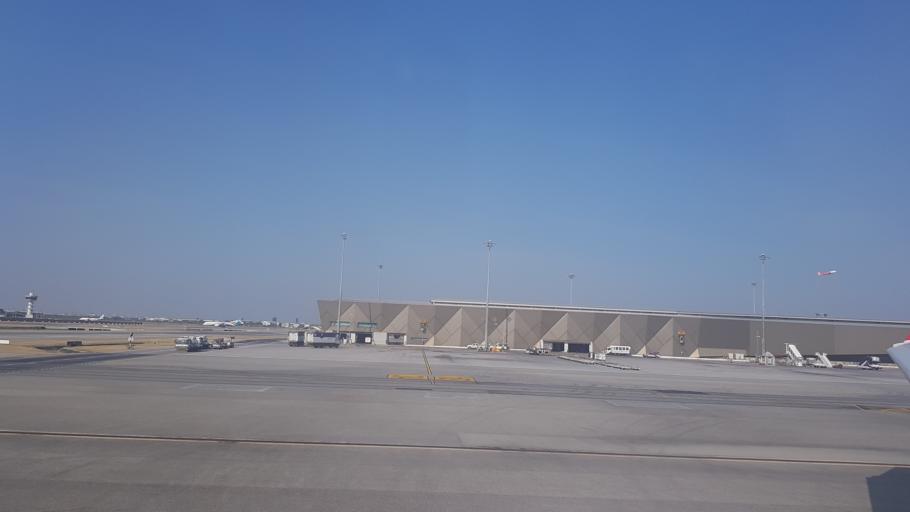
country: TH
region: Bangkok
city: Lat Krabang
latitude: 13.6869
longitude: 100.7516
